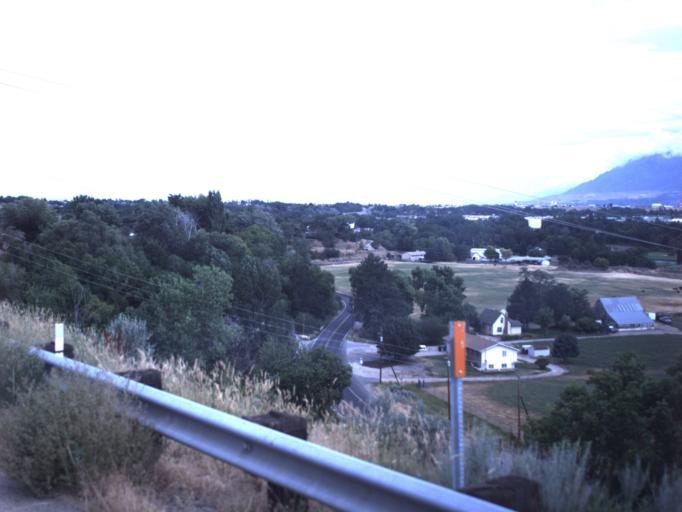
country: US
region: Utah
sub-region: Weber County
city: Riverdale
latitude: 41.1570
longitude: -112.0030
